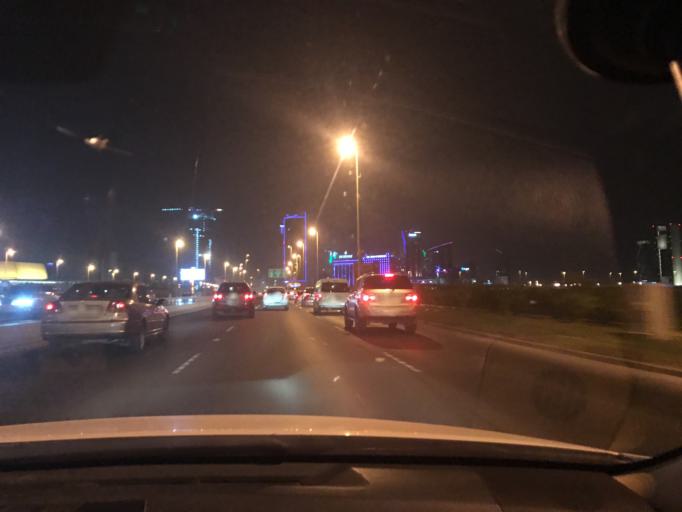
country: BH
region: Muharraq
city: Al Muharraq
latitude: 26.2465
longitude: 50.6014
